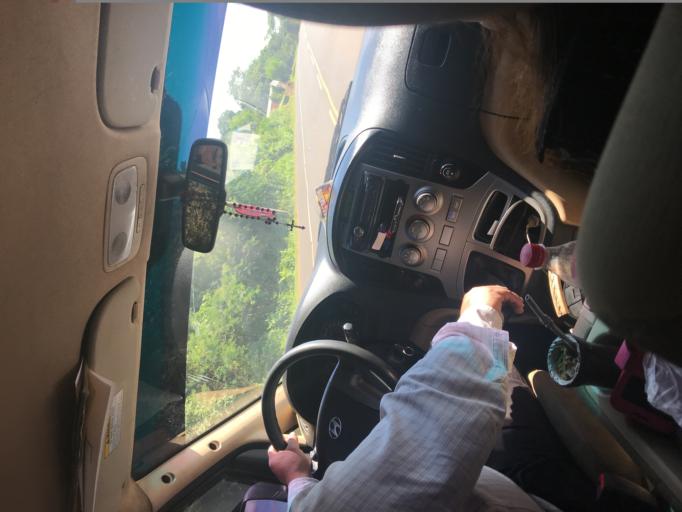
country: PY
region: San Pedro
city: Union
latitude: -24.6802
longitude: -56.4652
